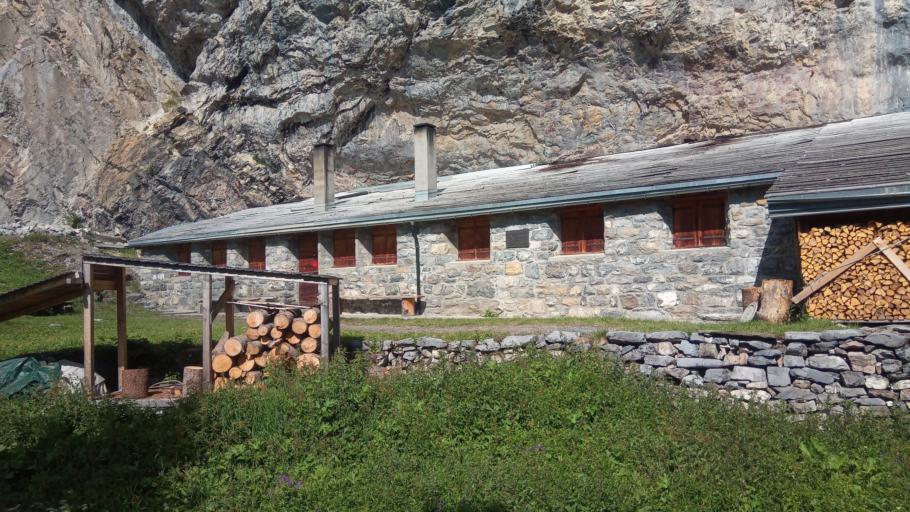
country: CH
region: Bern
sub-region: Frutigen-Niedersimmental District
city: Kandersteg
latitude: 46.4605
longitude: 7.6500
